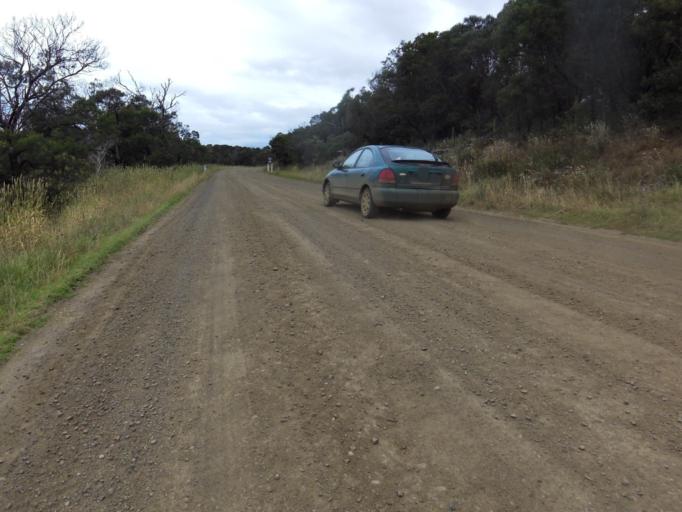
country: AU
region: Victoria
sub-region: Bass Coast
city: Cowes
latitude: -38.3805
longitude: 145.2790
